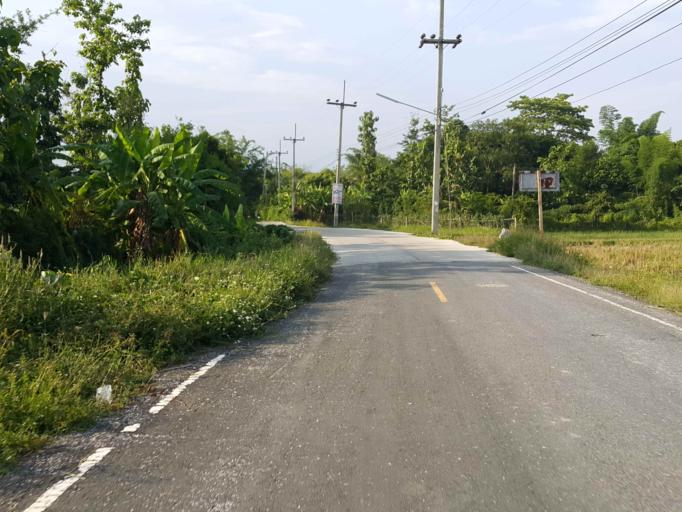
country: TH
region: Chiang Mai
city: San Sai
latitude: 18.8423
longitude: 99.0960
